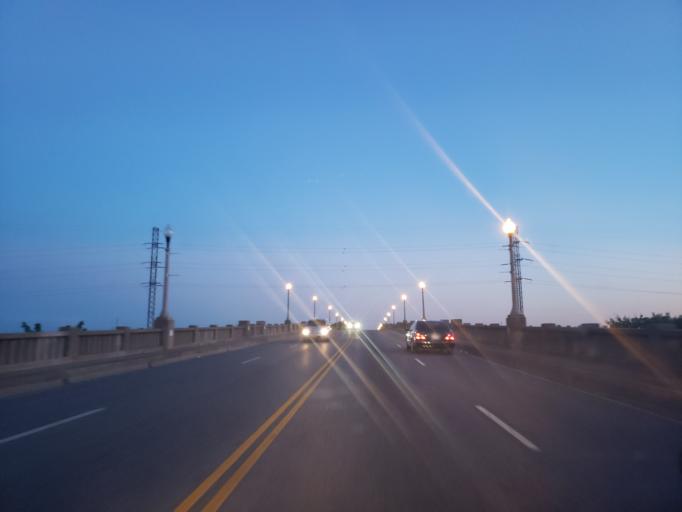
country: US
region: Texas
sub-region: Dallas County
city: Dallas
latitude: 32.7586
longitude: -96.7947
